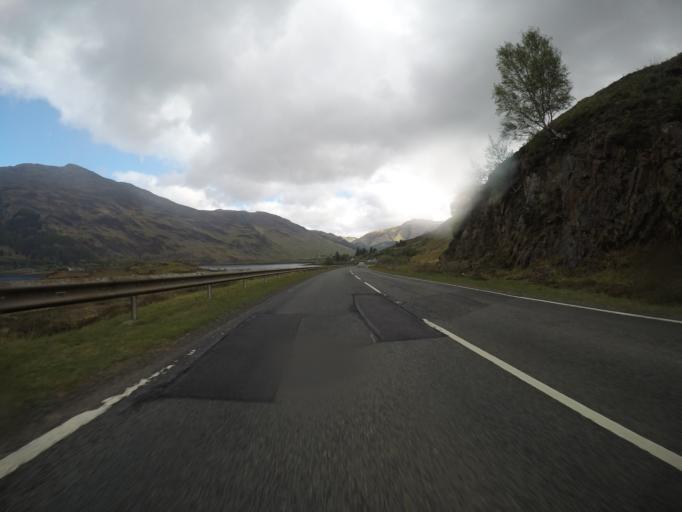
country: GB
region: Scotland
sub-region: Highland
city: Fort William
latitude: 57.2231
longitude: -5.4139
